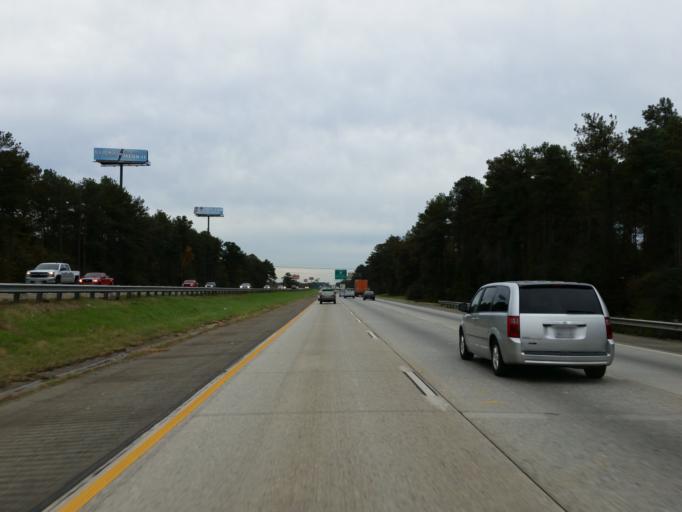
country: US
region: Georgia
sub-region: Peach County
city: Byron
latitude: 32.6328
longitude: -83.7435
